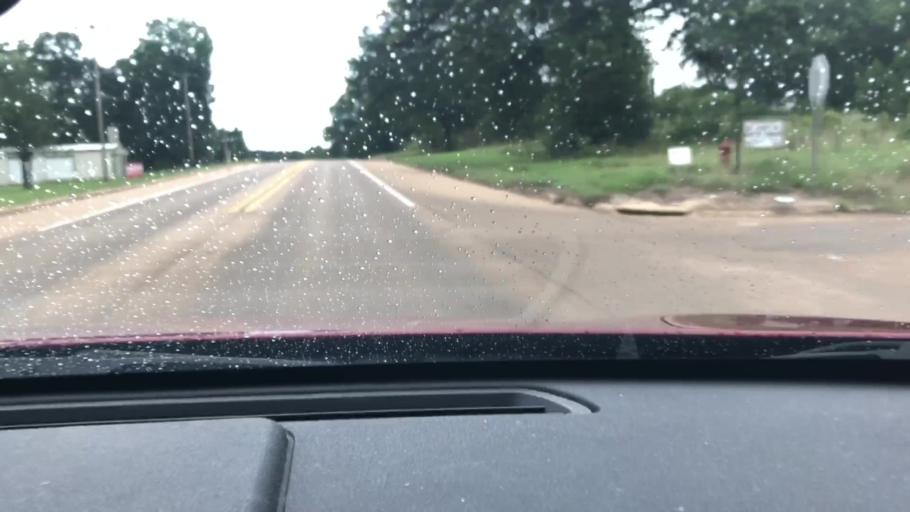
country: US
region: Arkansas
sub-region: Lafayette County
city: Stamps
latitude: 33.3585
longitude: -93.4371
